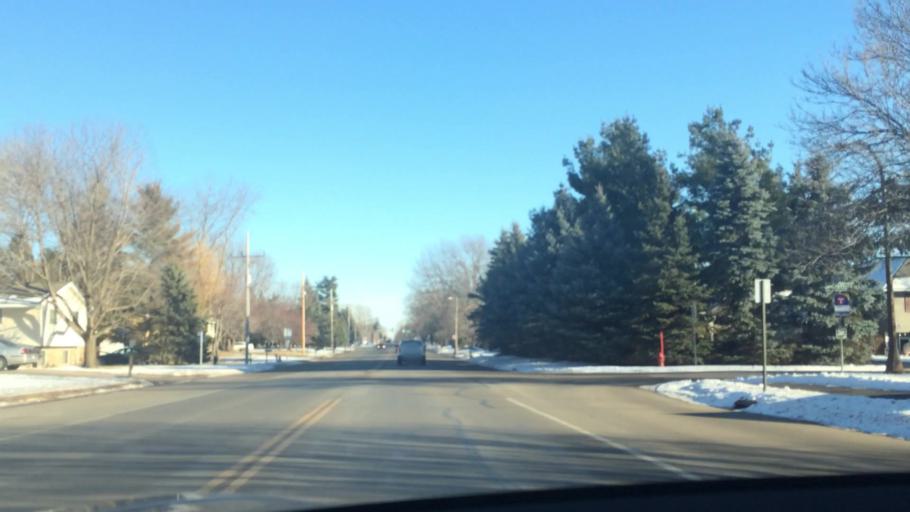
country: US
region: Minnesota
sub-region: Anoka County
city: Circle Pines
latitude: 45.1242
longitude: -93.1329
